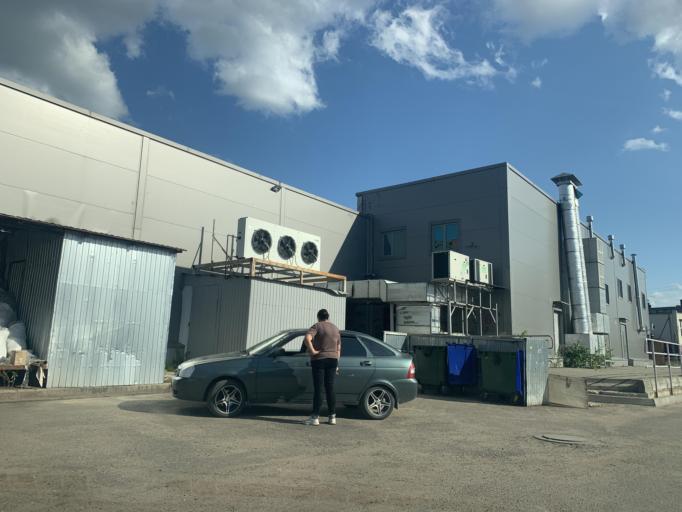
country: RU
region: Jaroslavl
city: Tutayev
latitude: 57.8624
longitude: 39.5084
